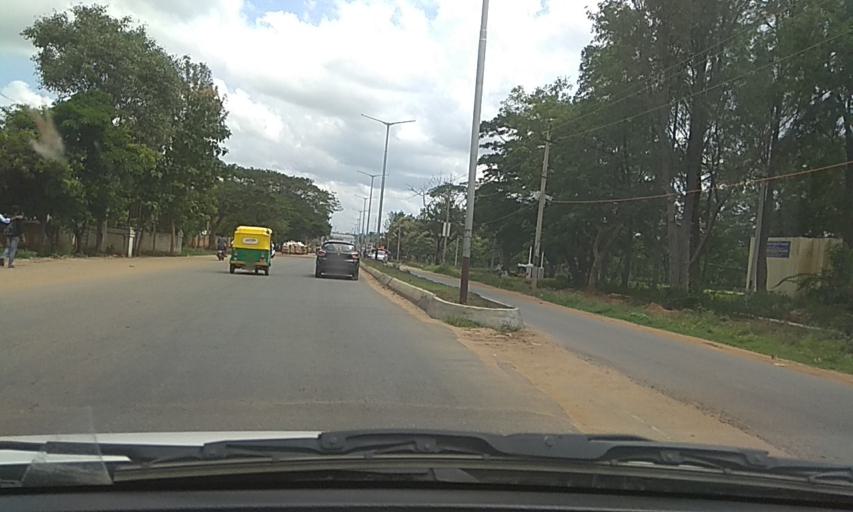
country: IN
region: Karnataka
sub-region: Tumkur
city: Tumkur
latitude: 13.3660
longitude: 77.1032
